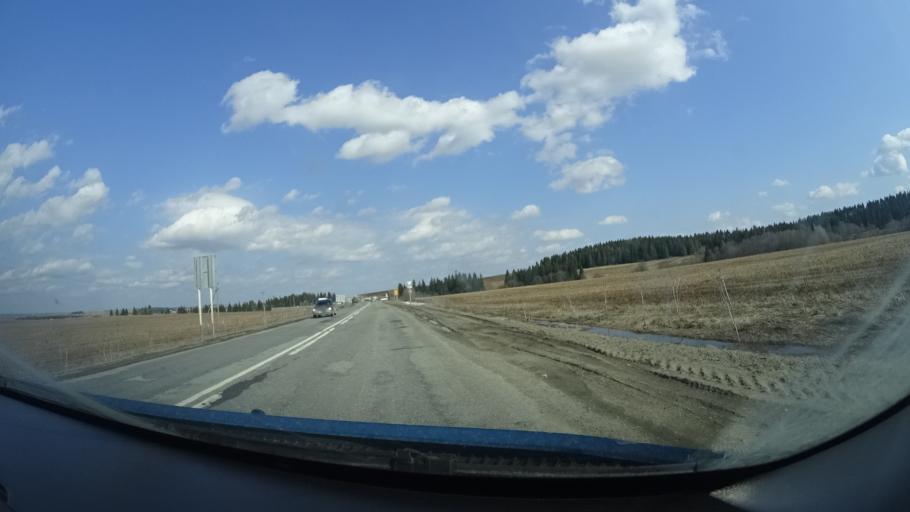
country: RU
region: Perm
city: Kultayevo
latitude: 57.8611
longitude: 55.8724
